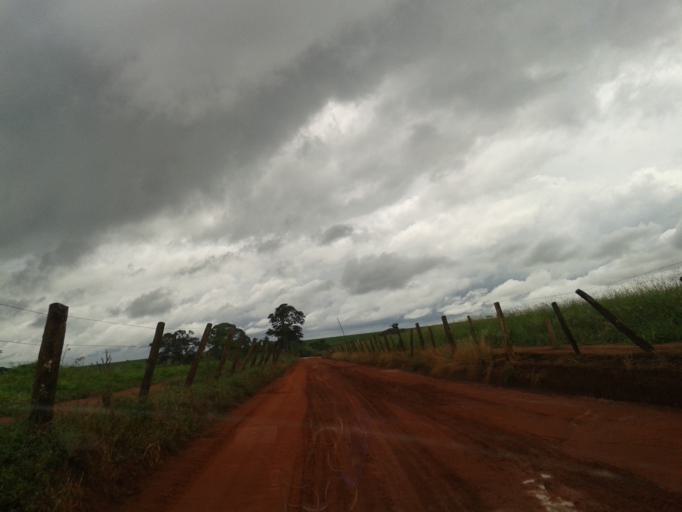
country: BR
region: Minas Gerais
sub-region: Santa Vitoria
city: Santa Vitoria
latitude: -18.6783
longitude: -49.9353
